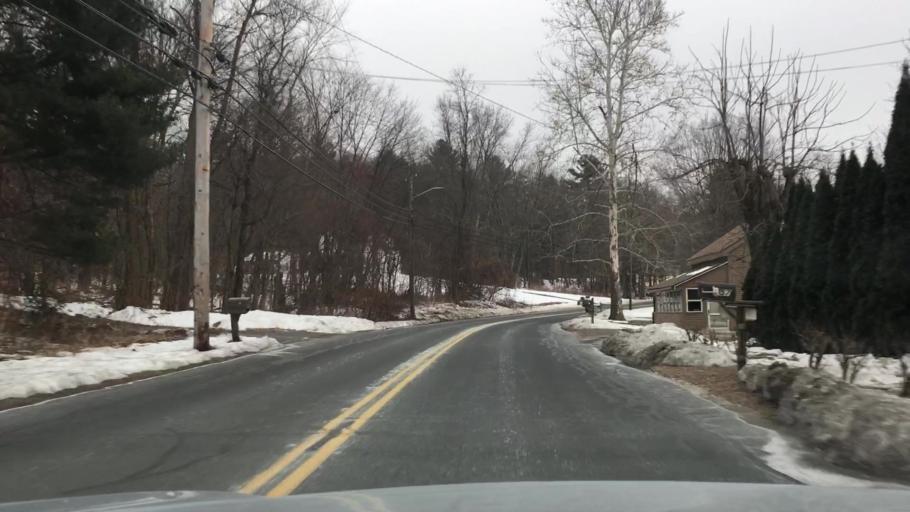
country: US
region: Massachusetts
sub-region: Hampden County
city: Westfield
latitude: 42.0948
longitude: -72.7111
